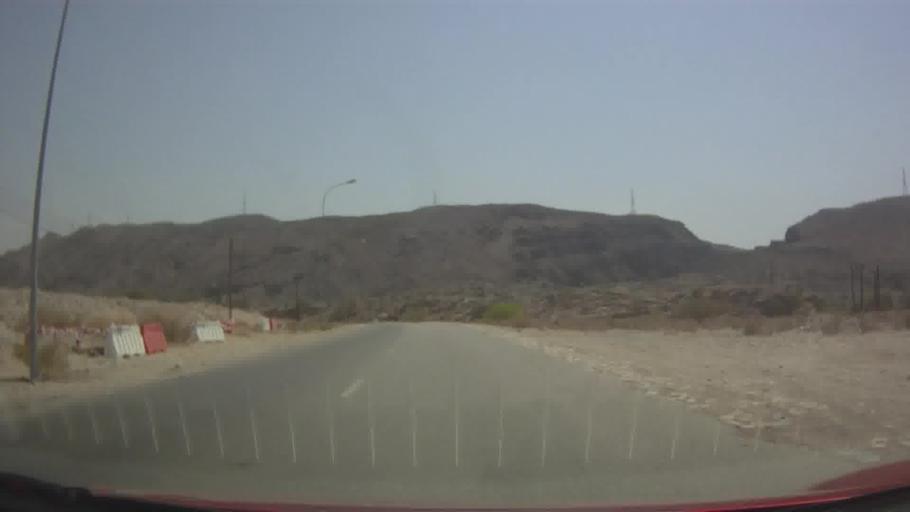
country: OM
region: Muhafazat Masqat
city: Muscat
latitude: 23.5115
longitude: 58.6349
